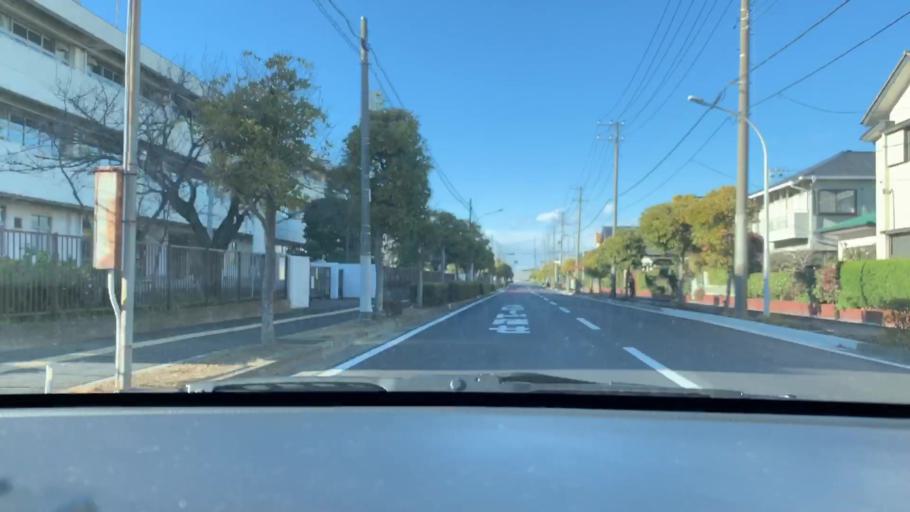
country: JP
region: Tokyo
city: Urayasu
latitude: 35.6382
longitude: 139.8976
